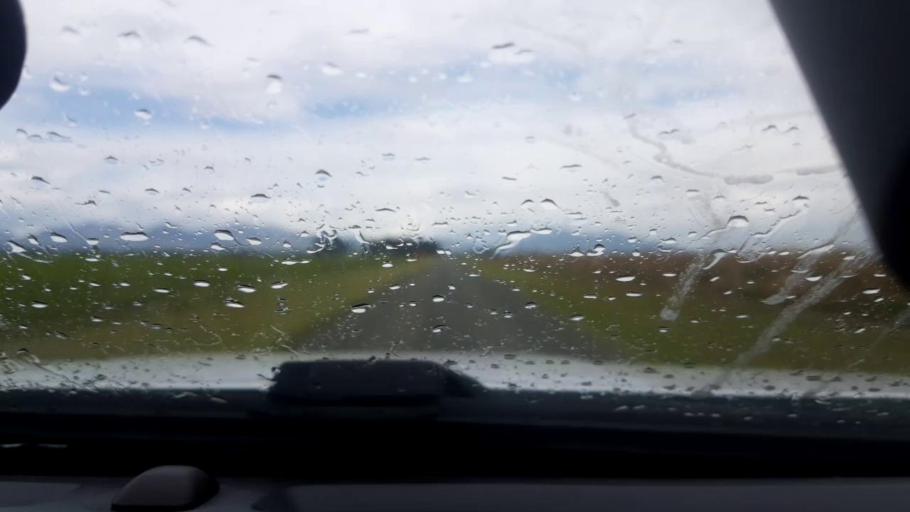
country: NZ
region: Canterbury
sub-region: Timaru District
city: Pleasant Point
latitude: -44.1158
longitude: 171.3564
